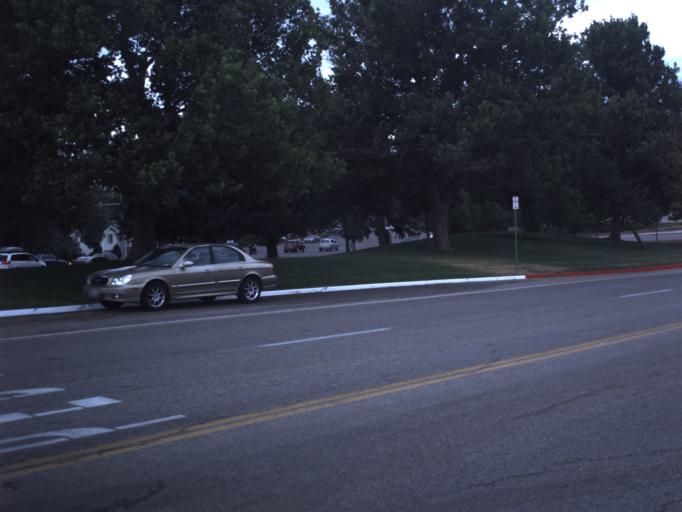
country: US
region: Utah
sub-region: Weber County
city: South Ogden
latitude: 41.1924
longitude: -111.9482
